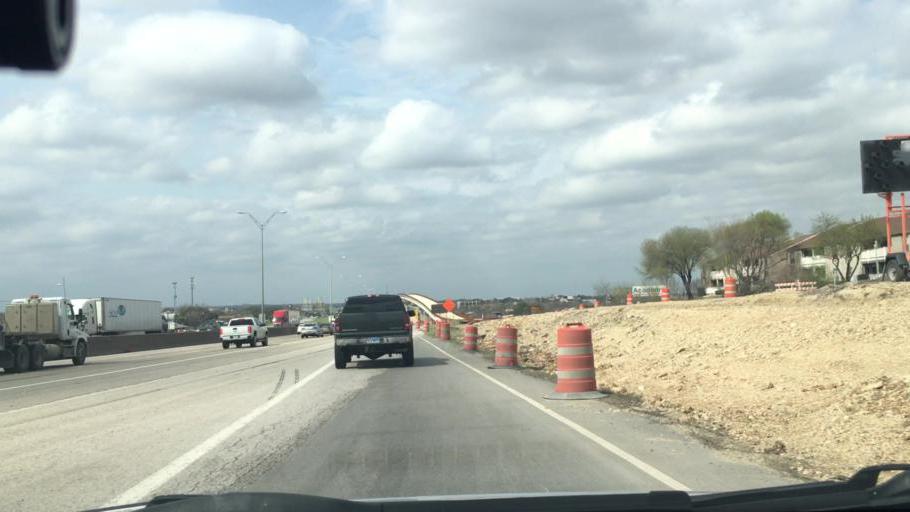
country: US
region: Texas
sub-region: Williamson County
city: Round Rock
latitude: 30.4956
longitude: -97.6788
